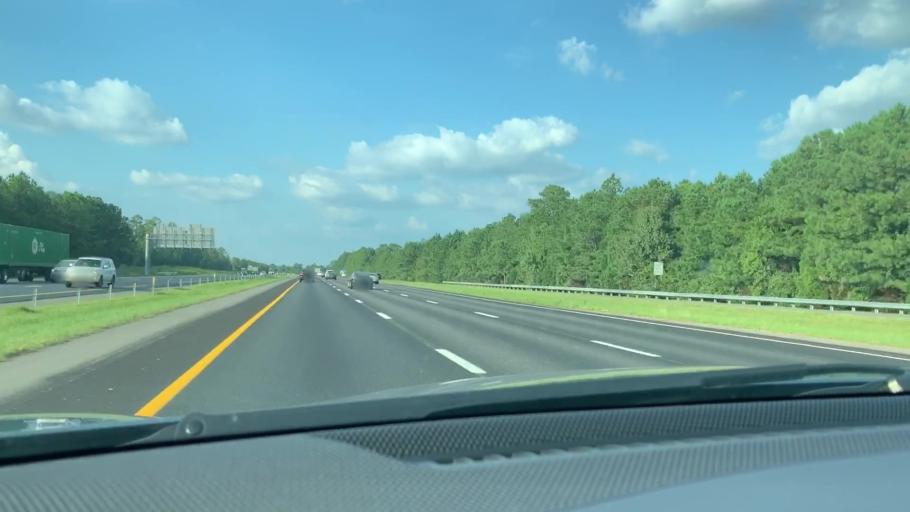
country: US
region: South Carolina
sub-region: Richland County
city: Forest Acres
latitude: 33.9801
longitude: -80.9541
